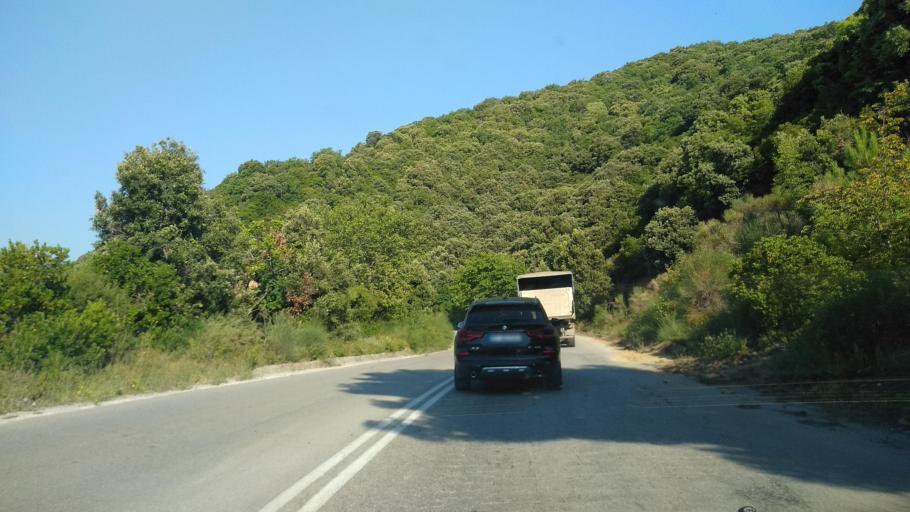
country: GR
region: Central Macedonia
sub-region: Nomos Chalkidikis
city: Stratonion
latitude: 40.5198
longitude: 23.8180
